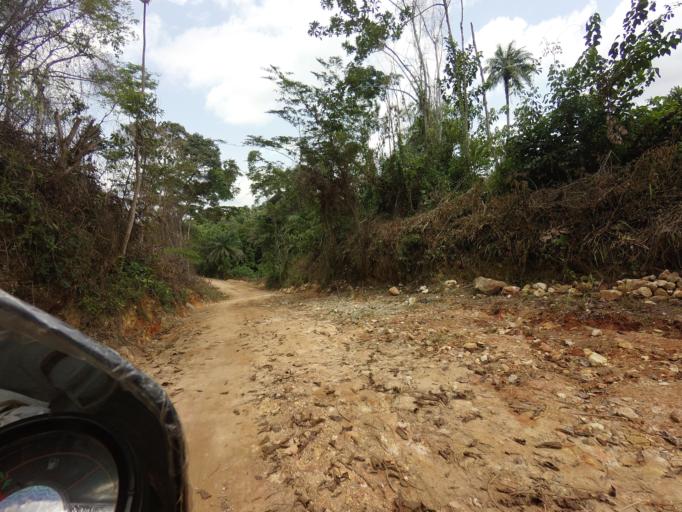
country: SL
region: Eastern Province
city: Kailahun
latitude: 8.3619
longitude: -10.7160
